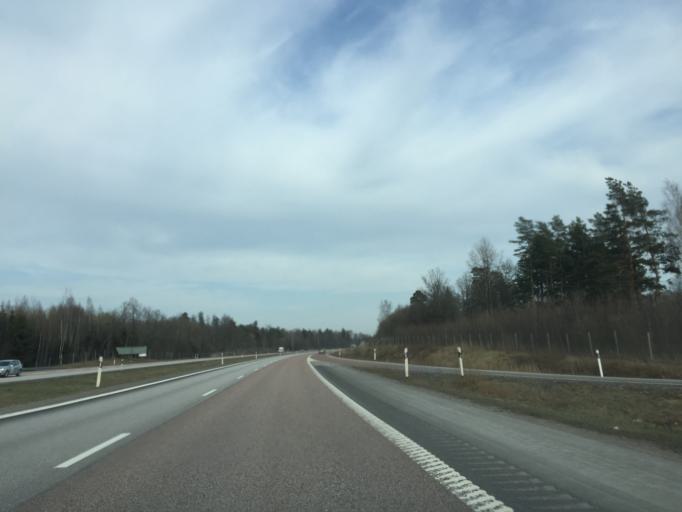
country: SE
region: OErebro
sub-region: Orebro Kommun
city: Orebro
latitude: 59.3048
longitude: 15.2610
